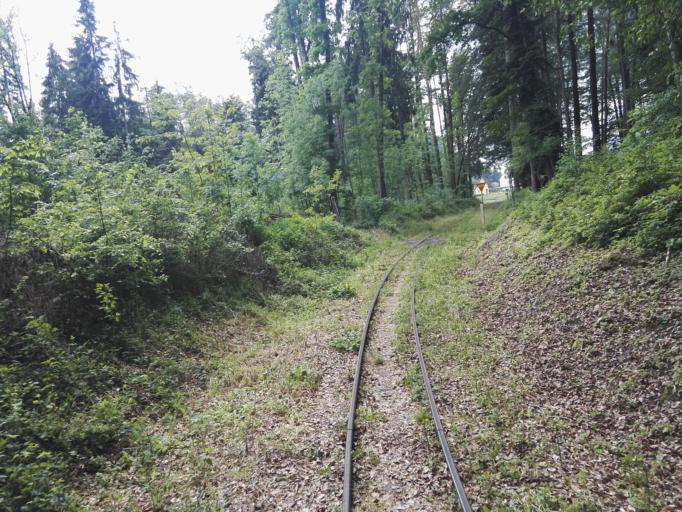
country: AT
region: Styria
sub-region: Politischer Bezirk Weiz
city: Krottendorf
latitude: 47.2194
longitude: 15.6608
